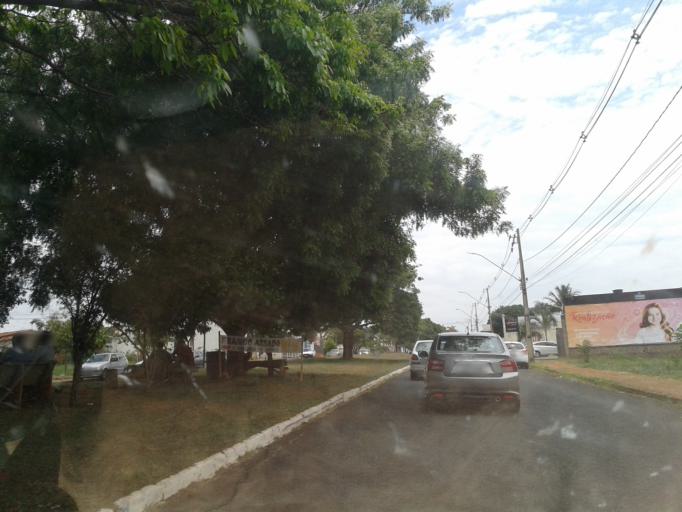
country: BR
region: Minas Gerais
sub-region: Uberlandia
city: Uberlandia
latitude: -18.9136
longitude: -48.3151
